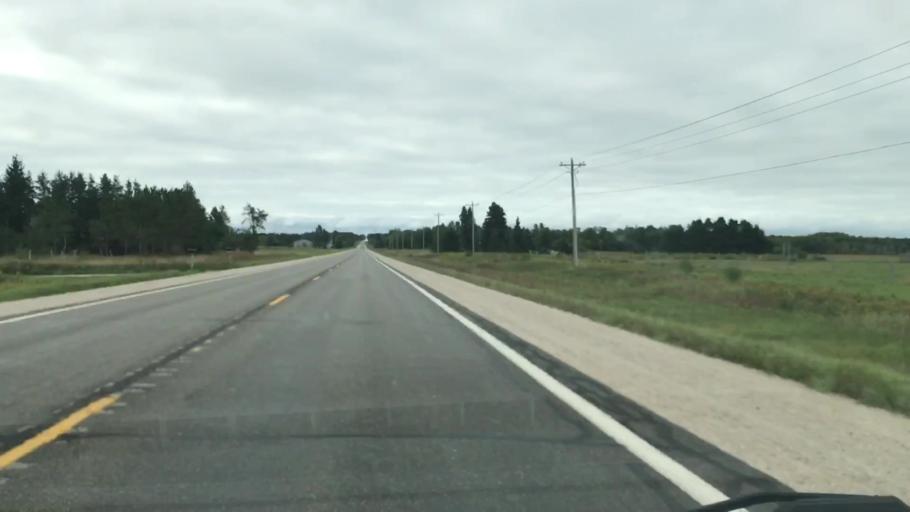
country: US
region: Michigan
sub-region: Luce County
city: Newberry
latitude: 46.1443
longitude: -85.5713
